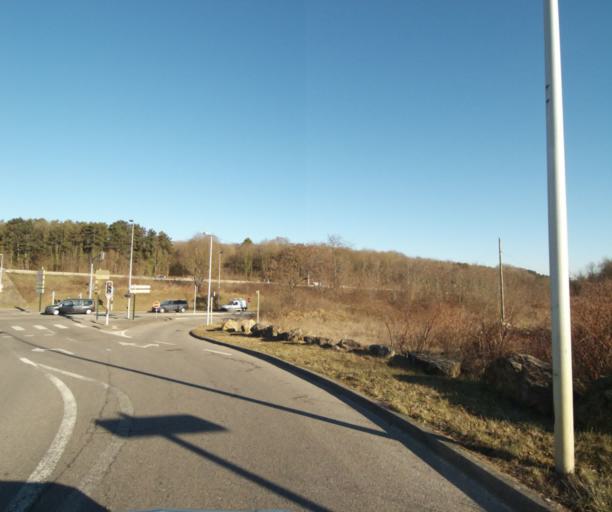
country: FR
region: Lorraine
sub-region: Departement de Meurthe-et-Moselle
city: Laxou
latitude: 48.7057
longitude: 6.1404
